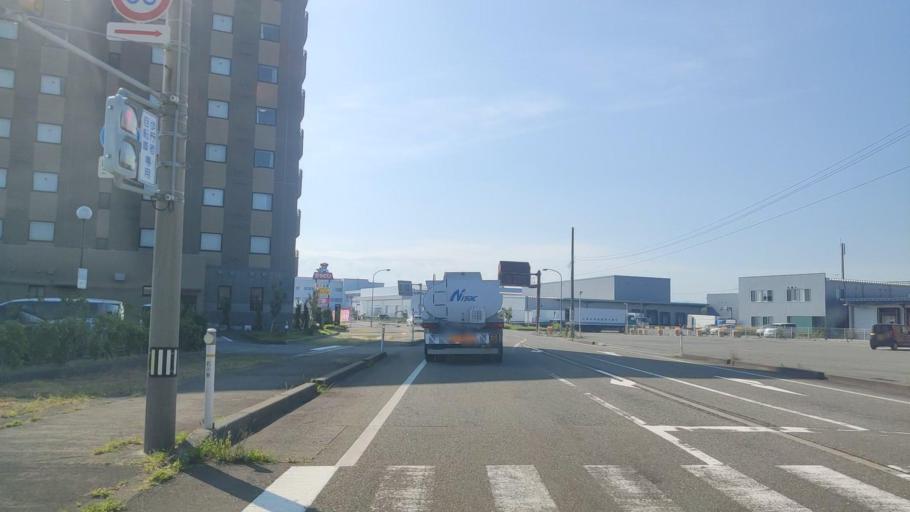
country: JP
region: Ishikawa
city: Matsuto
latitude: 36.5022
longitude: 136.5011
